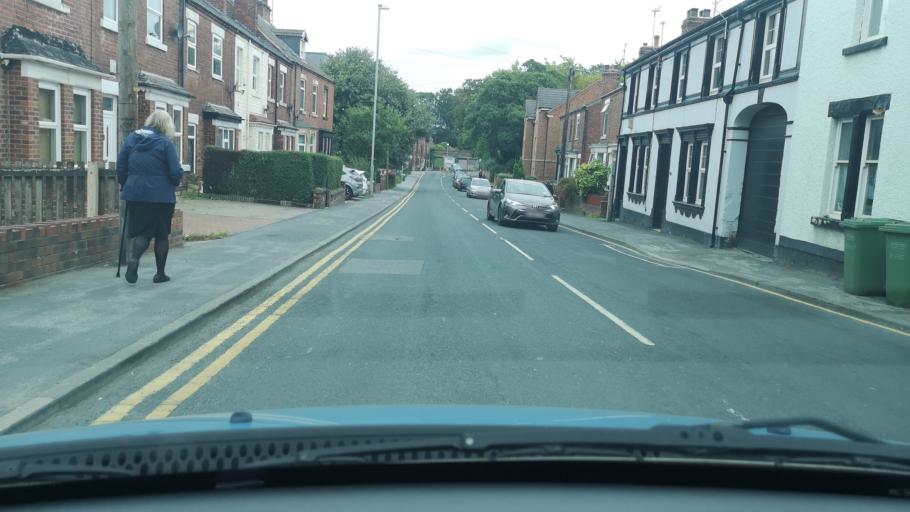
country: GB
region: England
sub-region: City and Borough of Wakefield
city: Pontefract
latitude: 53.6944
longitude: -1.3079
